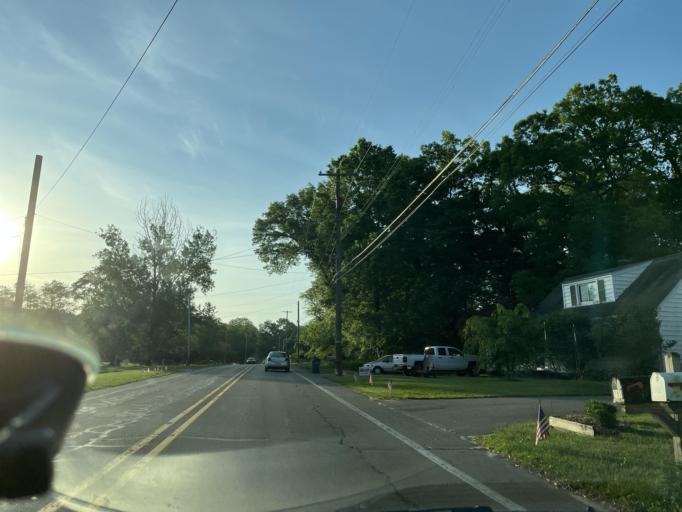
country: US
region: Michigan
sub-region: Barry County
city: Middleville
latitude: 42.7137
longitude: -85.4572
